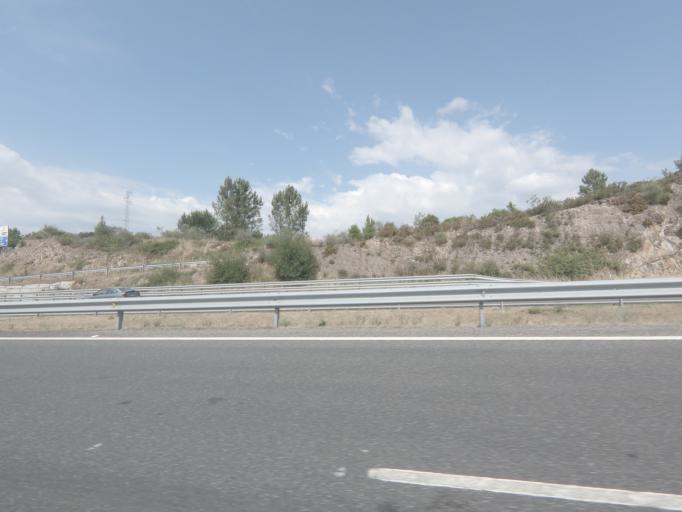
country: ES
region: Galicia
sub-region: Provincia de Ourense
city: Ourense
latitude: 42.3054
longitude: -7.8750
